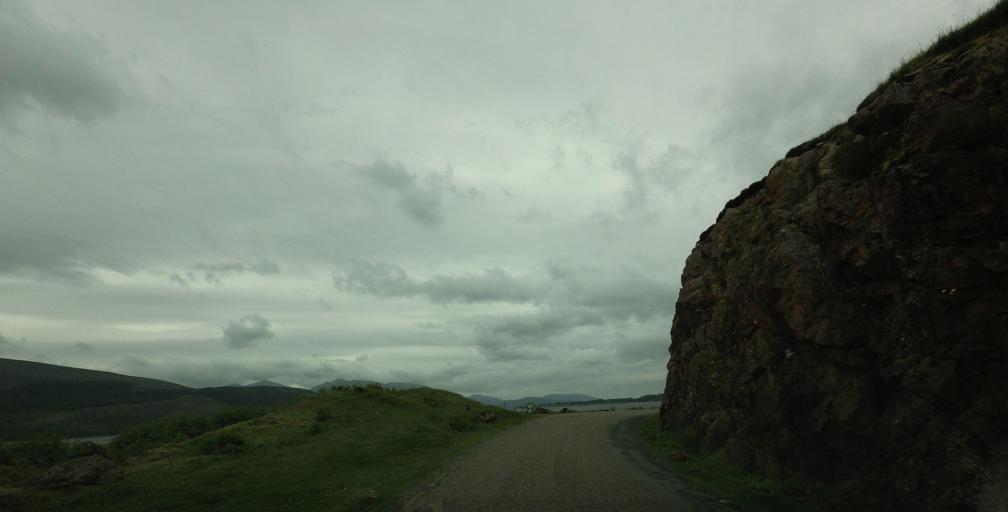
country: GB
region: Scotland
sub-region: Highland
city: Fort William
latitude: 56.7512
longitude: -5.2313
